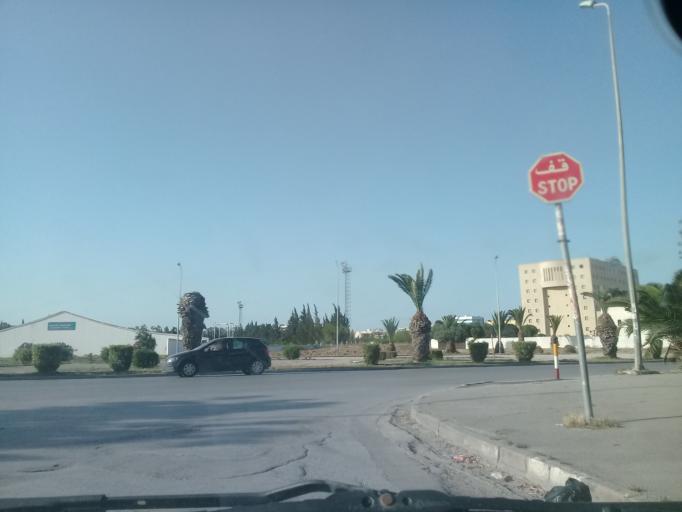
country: TN
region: Ariana
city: Ariana
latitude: 36.8394
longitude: 10.1932
